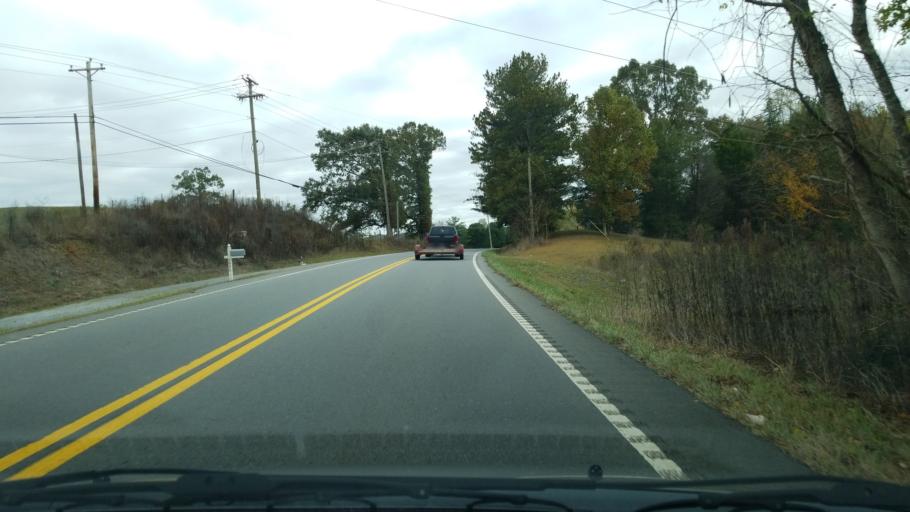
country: US
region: Tennessee
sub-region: Bradley County
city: Hopewell
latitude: 35.3221
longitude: -84.9671
